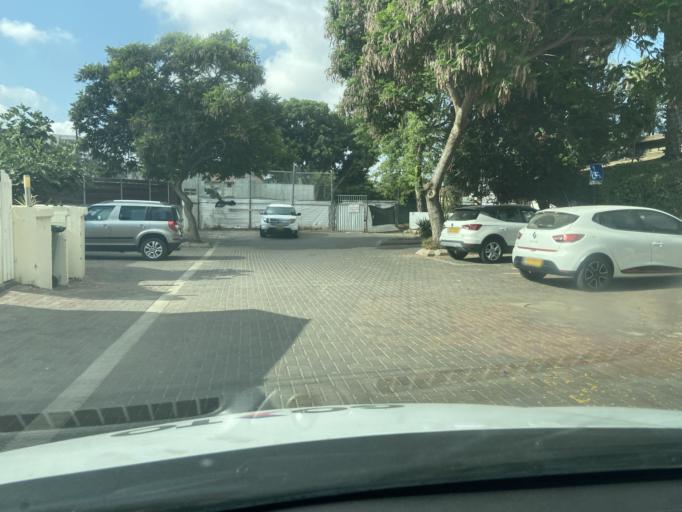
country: IL
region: Central District
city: Yehud
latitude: 32.0355
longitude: 34.8851
